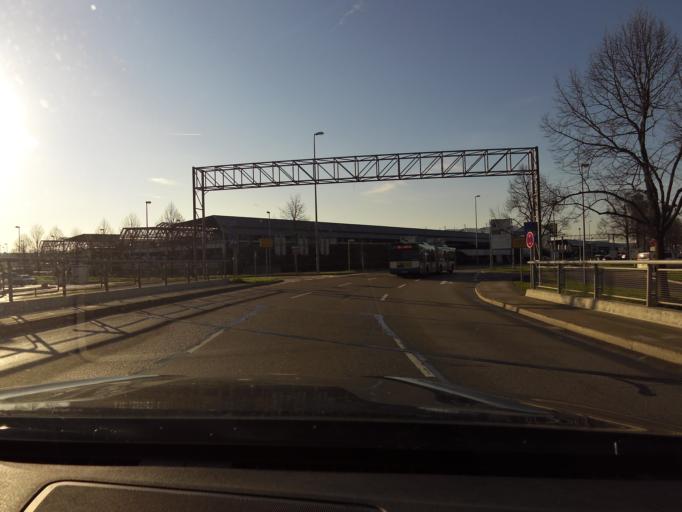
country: DE
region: Bavaria
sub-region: Upper Bavaria
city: Hallbergmoos
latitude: 48.3586
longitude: 11.7838
